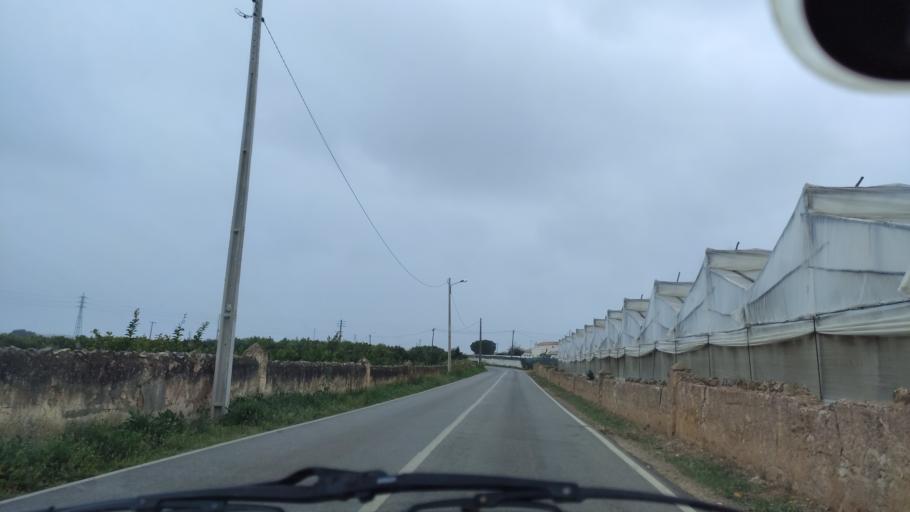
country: PT
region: Faro
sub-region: Faro
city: Santa Barbara de Nexe
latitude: 37.0736
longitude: -7.9433
